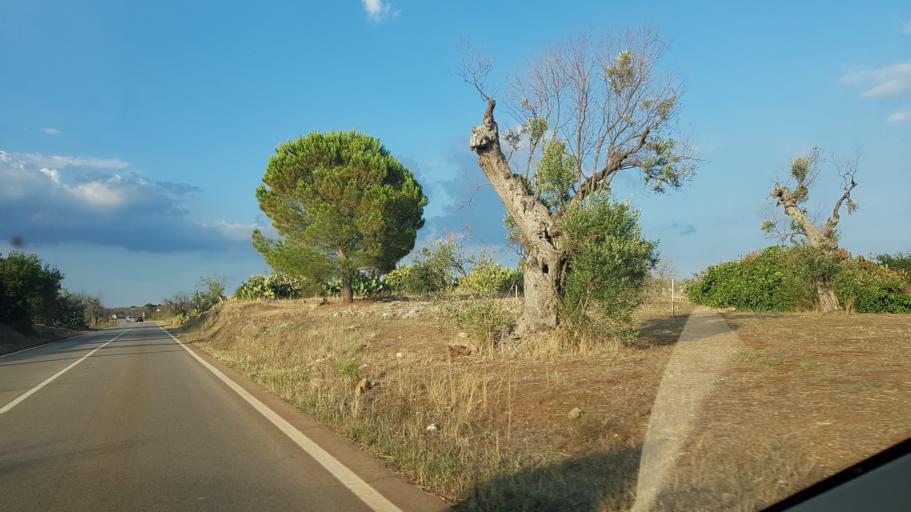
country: IT
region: Apulia
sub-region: Provincia di Lecce
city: Acquarica del Capo
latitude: 39.8880
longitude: 18.2412
